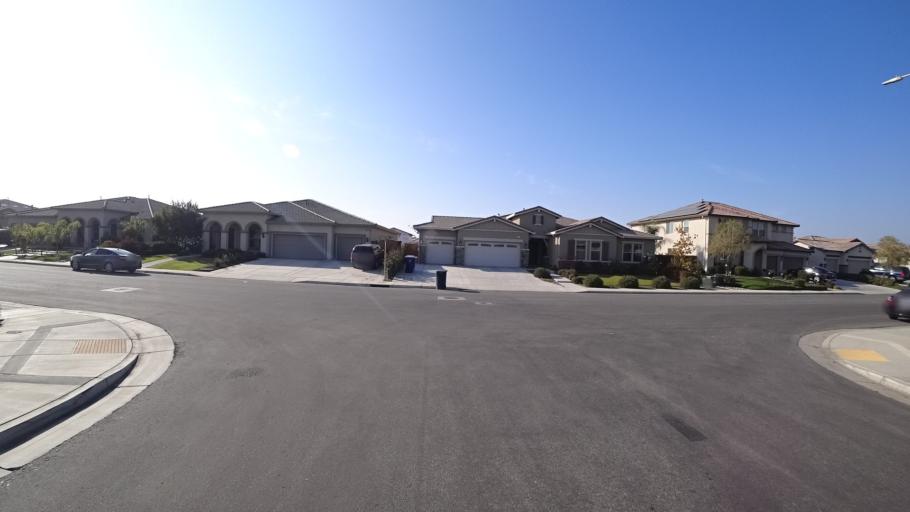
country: US
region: California
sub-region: Kern County
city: Rosedale
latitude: 35.3484
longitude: -119.1723
